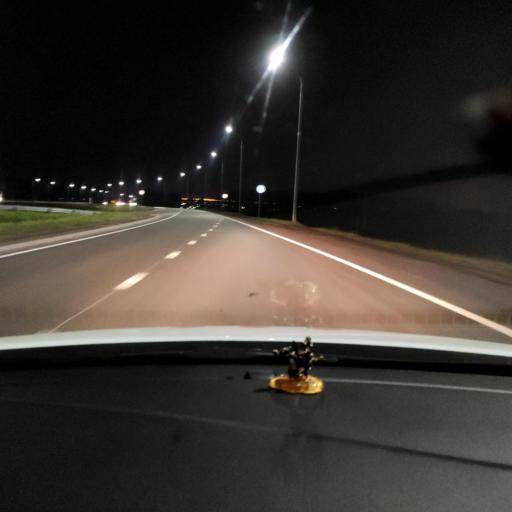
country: RU
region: Tatarstan
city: Vysokaya Gora
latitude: 55.8136
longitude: 49.4353
